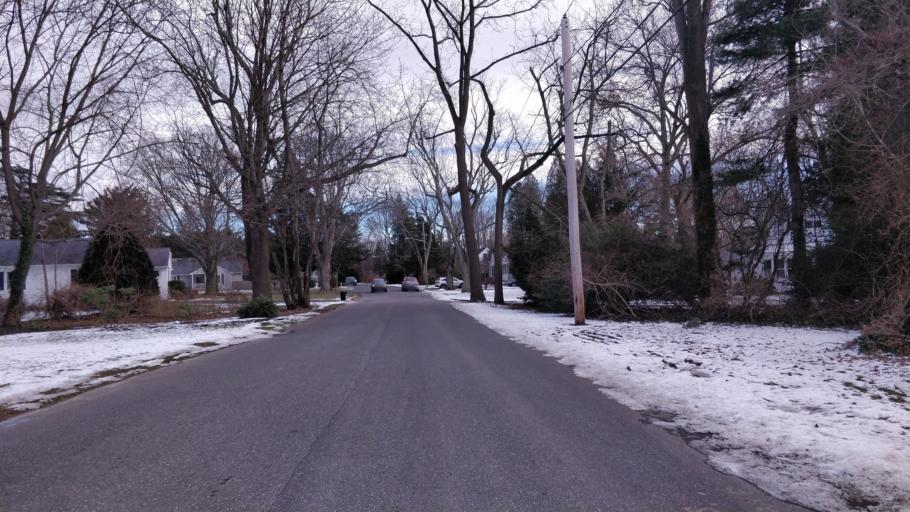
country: US
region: New York
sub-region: Suffolk County
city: Greenlawn
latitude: 40.8748
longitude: -73.3638
